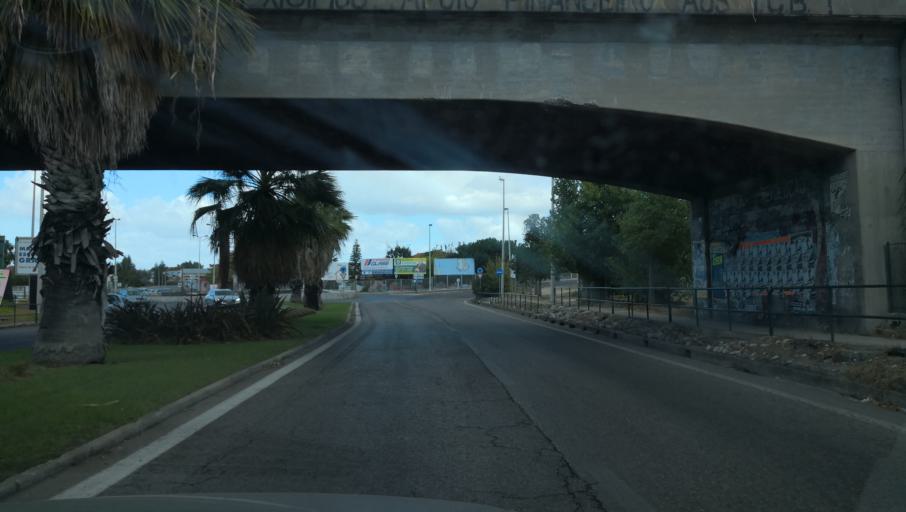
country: PT
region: Setubal
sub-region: Barreiro
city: Barreiro
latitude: 38.6611
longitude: -9.0545
